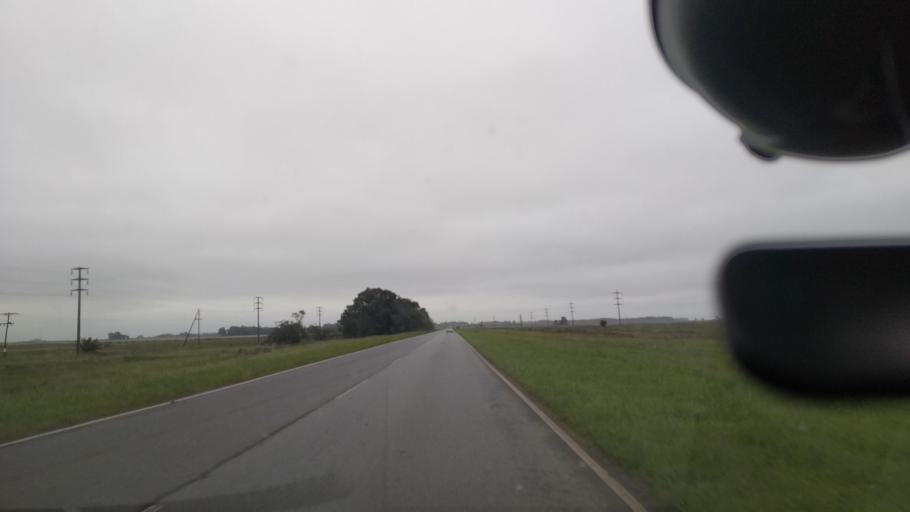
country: AR
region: Buenos Aires
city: Veronica
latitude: -35.3605
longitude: -57.4015
